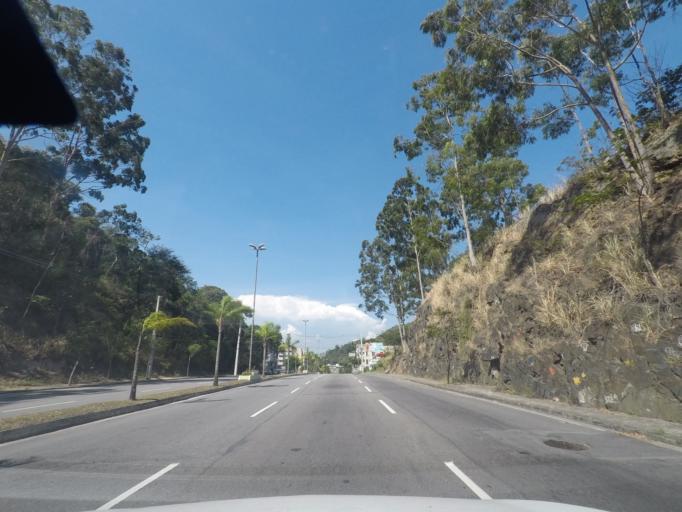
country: BR
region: Rio de Janeiro
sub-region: Niteroi
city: Niteroi
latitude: -22.9201
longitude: -43.0530
